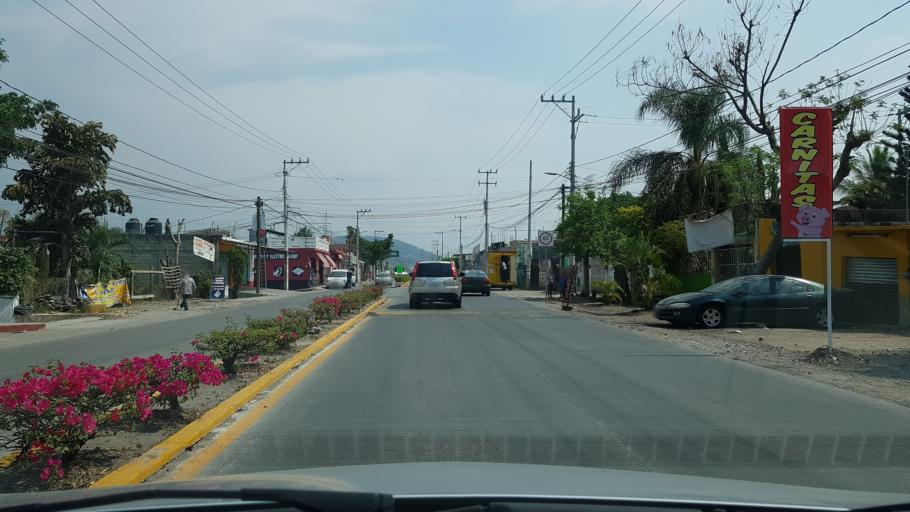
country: MX
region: Morelos
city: Emiliano Zapata
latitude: 18.8191
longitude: -99.1907
